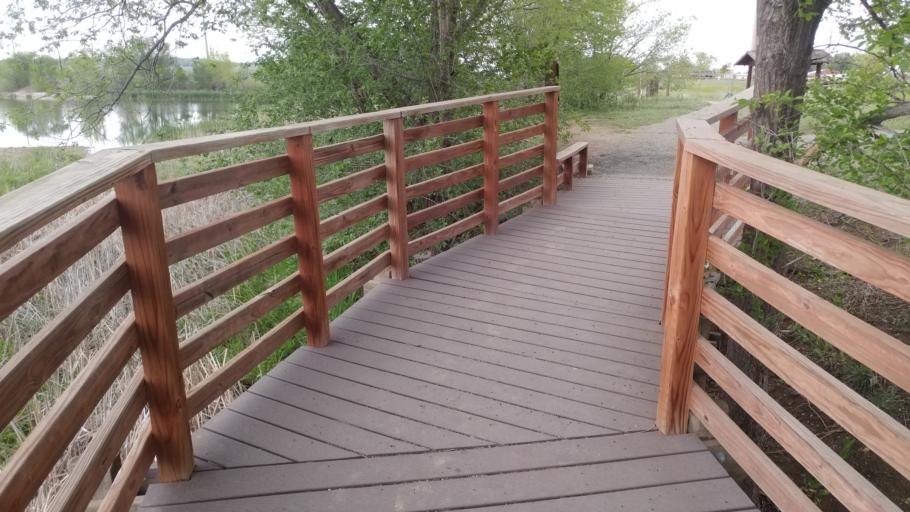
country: US
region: Colorado
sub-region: Boulder County
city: Gunbarrel
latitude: 40.0439
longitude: -105.1848
